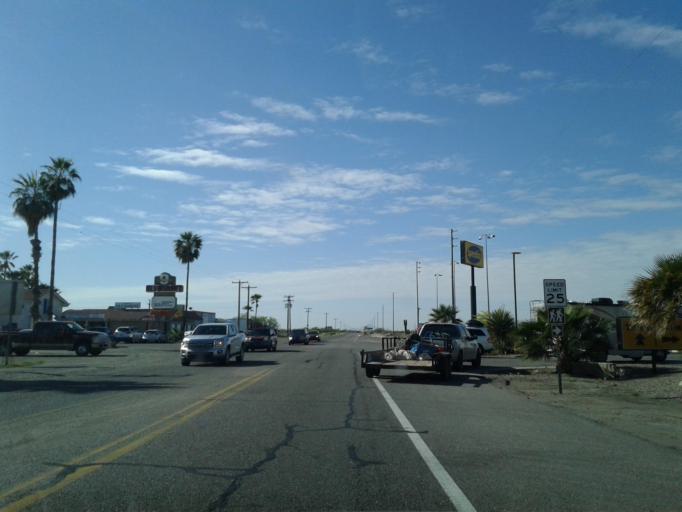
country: US
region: Arizona
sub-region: Pinal County
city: Arizona City
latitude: 32.8067
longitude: -111.6711
